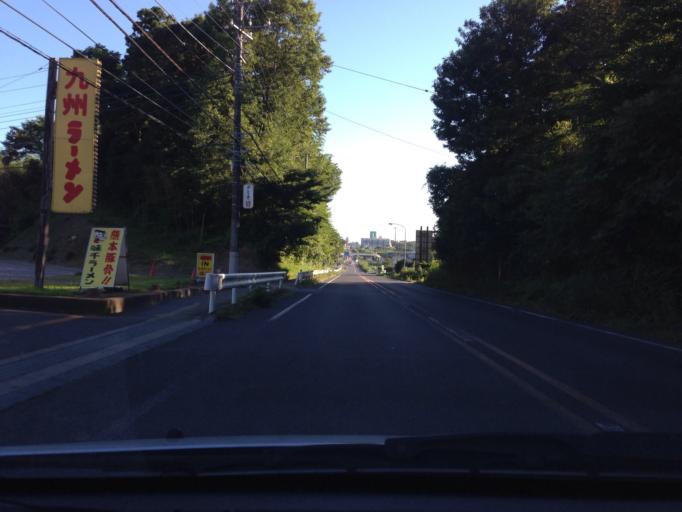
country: JP
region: Ibaraki
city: Naka
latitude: 36.0605
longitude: 140.1802
